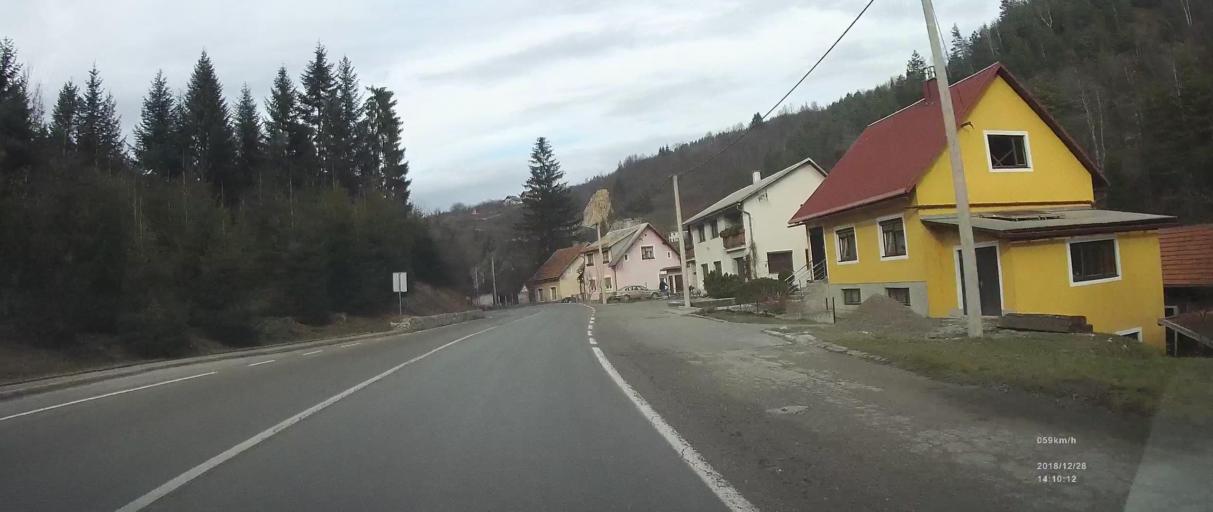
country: SI
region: Kostel
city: Kostel
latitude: 45.4518
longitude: 14.9772
